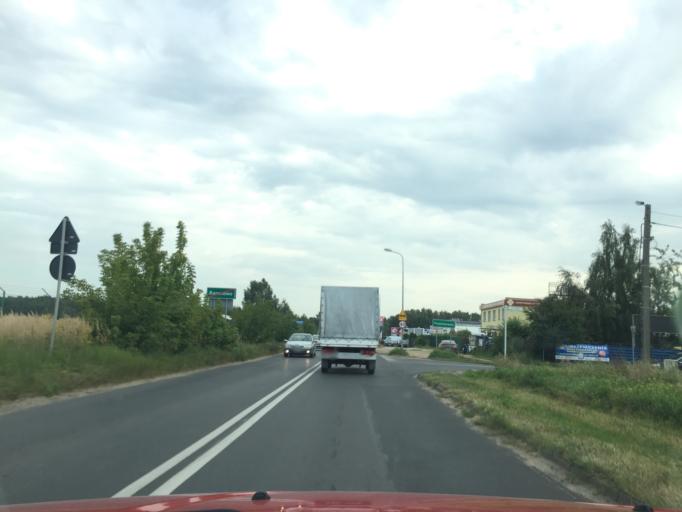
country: PL
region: Greater Poland Voivodeship
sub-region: Powiat poznanski
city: Baranowo
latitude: 52.4250
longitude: 16.7985
